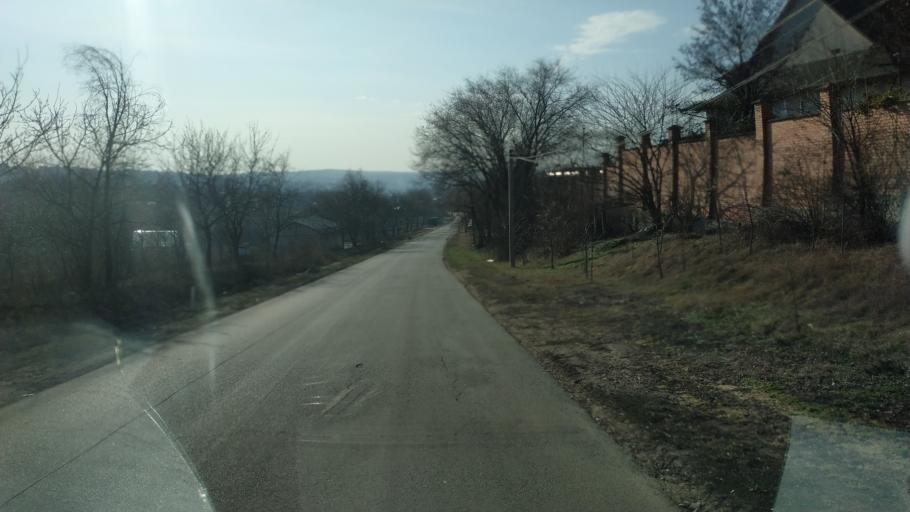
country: MD
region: Chisinau
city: Singera
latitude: 46.8401
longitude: 29.0273
